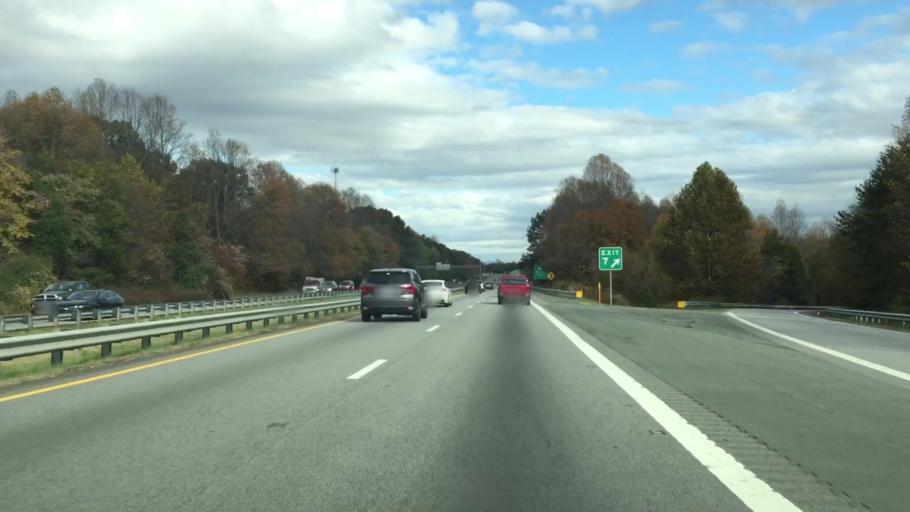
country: US
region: North Carolina
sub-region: Forsyth County
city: Winston-Salem
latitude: 36.0974
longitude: -80.2090
